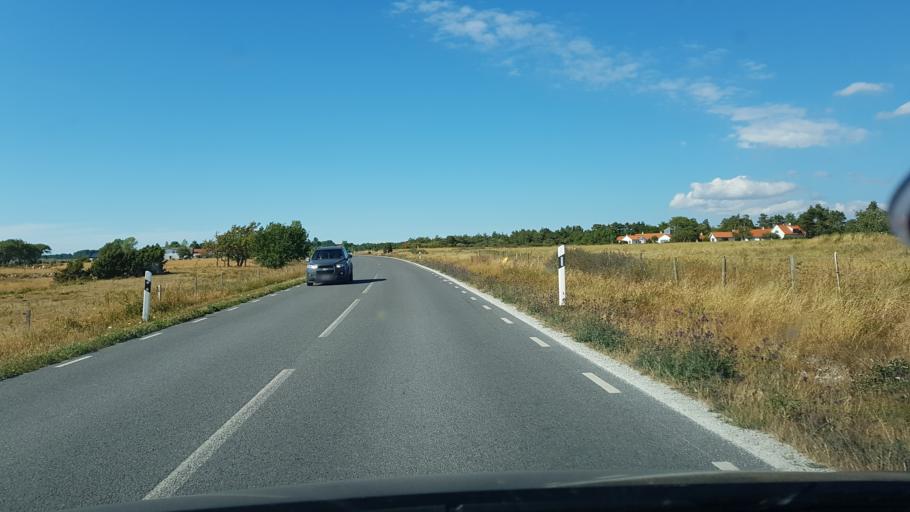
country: SE
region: Gotland
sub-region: Gotland
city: Klintehamn
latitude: 57.4264
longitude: 18.1496
